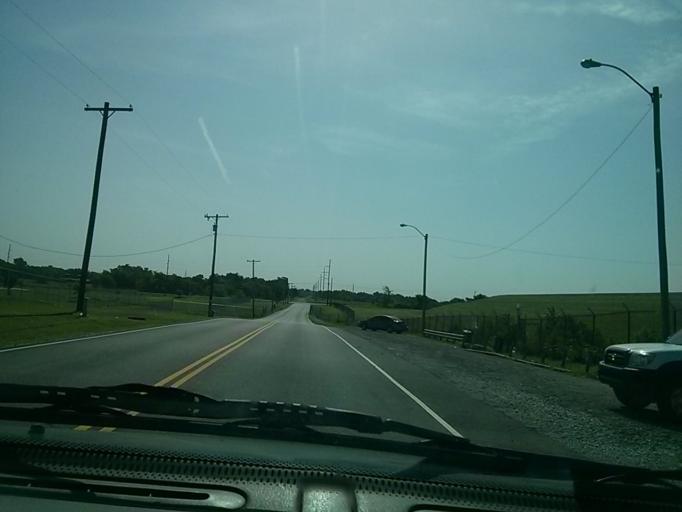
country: US
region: Oklahoma
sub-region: Rogers County
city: Catoosa
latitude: 36.1335
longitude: -95.7653
